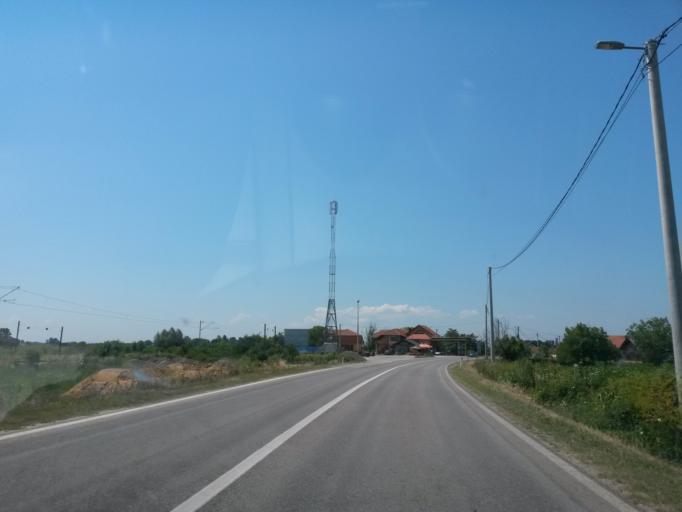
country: BA
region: Republika Srpska
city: Bosanski Samac
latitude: 45.0434
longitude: 18.4544
